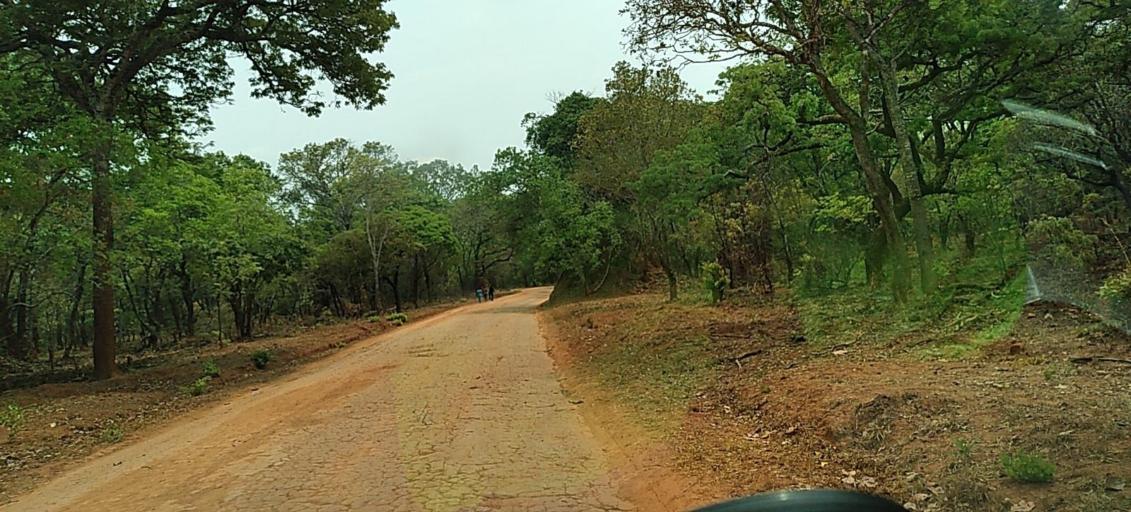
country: ZM
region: North-Western
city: Solwezi
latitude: -12.8276
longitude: 26.5370
